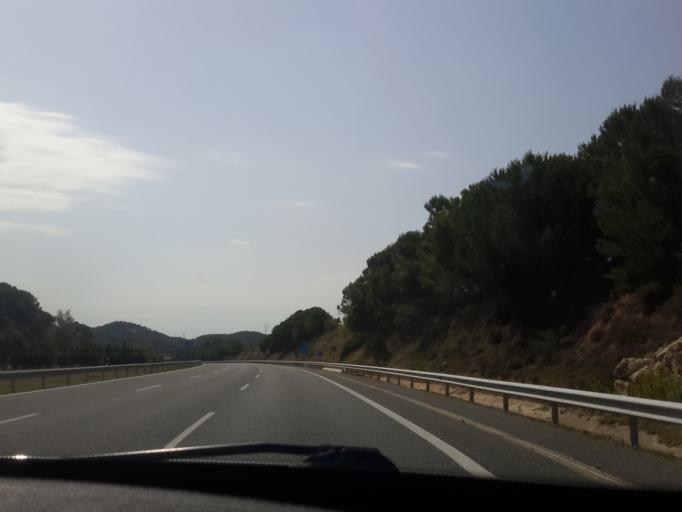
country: ES
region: Catalonia
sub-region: Provincia de Tarragona
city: Vimbodi
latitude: 41.4116
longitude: 1.0515
